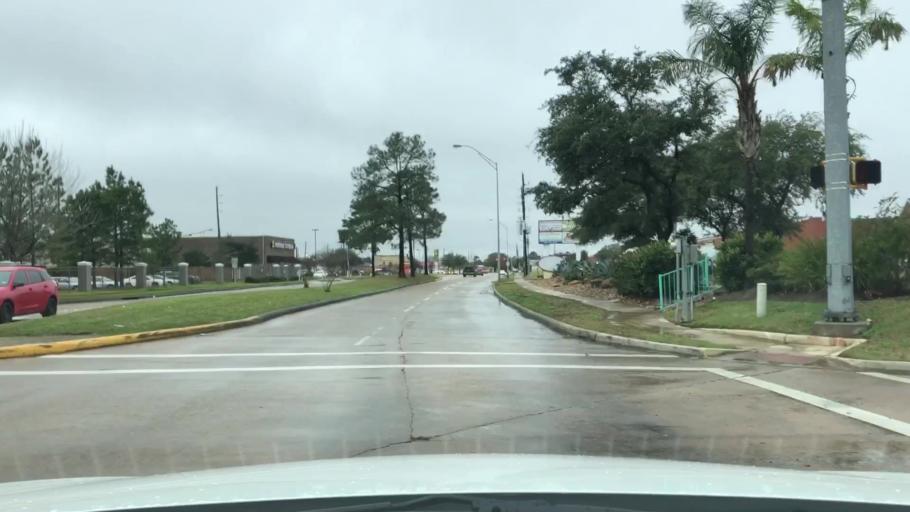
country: US
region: Texas
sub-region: Fort Bend County
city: Cinco Ranch
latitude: 29.7749
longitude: -95.7484
